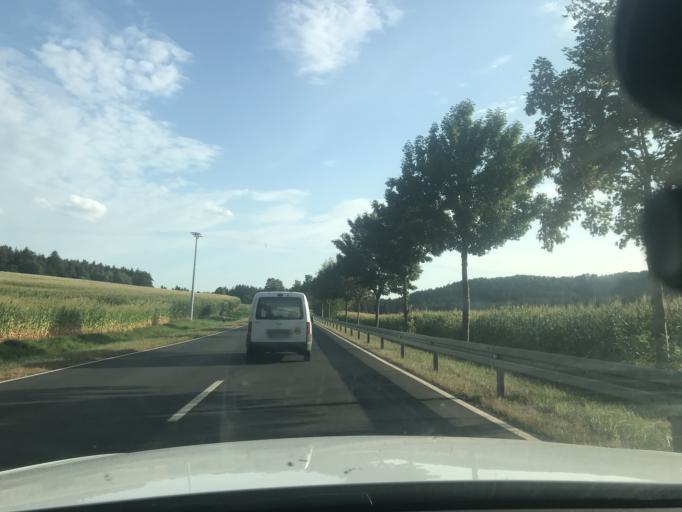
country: DE
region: Bavaria
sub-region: Upper Franconia
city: Pegnitz
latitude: 49.7987
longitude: 11.5801
